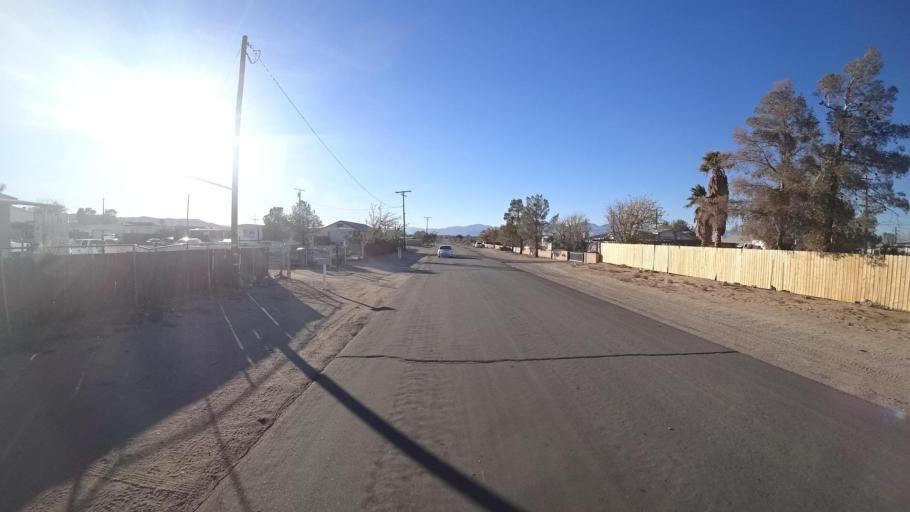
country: US
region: California
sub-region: Kern County
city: Ridgecrest
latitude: 35.6007
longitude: -117.6551
